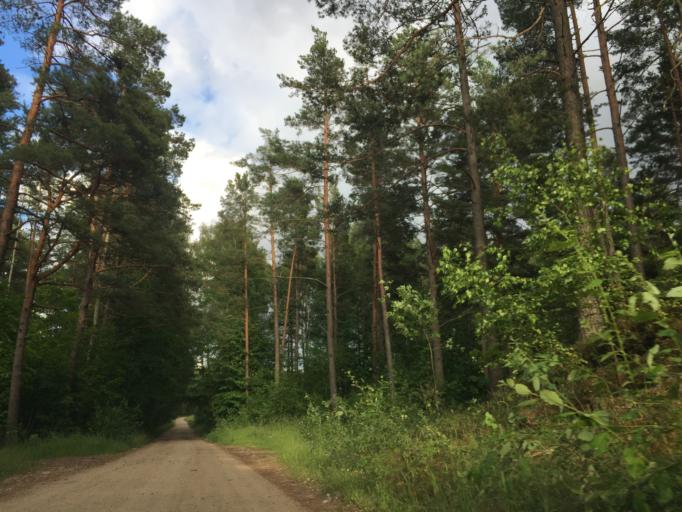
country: LV
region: Carnikava
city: Carnikava
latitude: 57.1728
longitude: 24.3465
